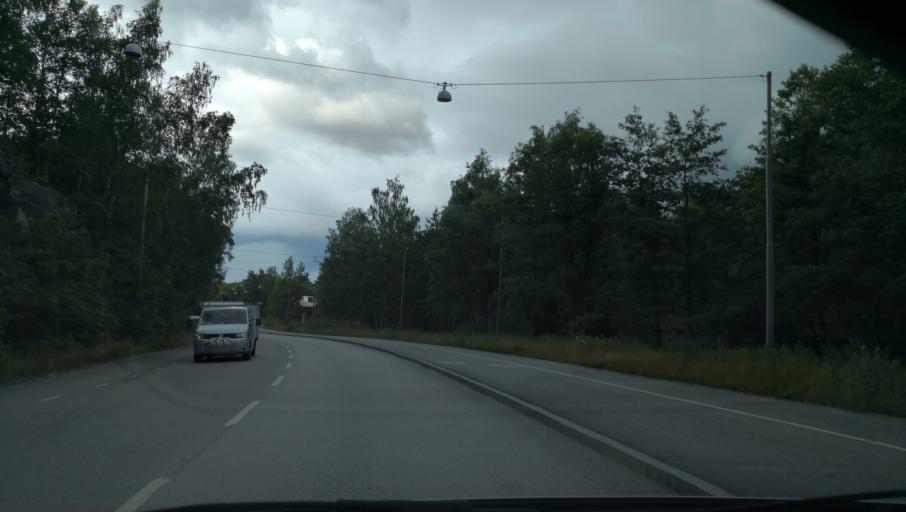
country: SE
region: Stockholm
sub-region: Nacka Kommun
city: Alta
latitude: 59.2388
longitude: 18.1197
